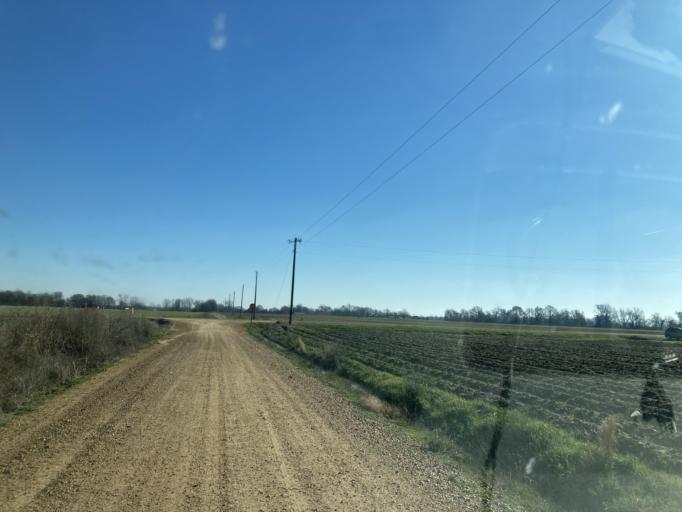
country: US
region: Mississippi
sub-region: Yazoo County
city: Yazoo City
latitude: 32.9666
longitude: -90.6062
